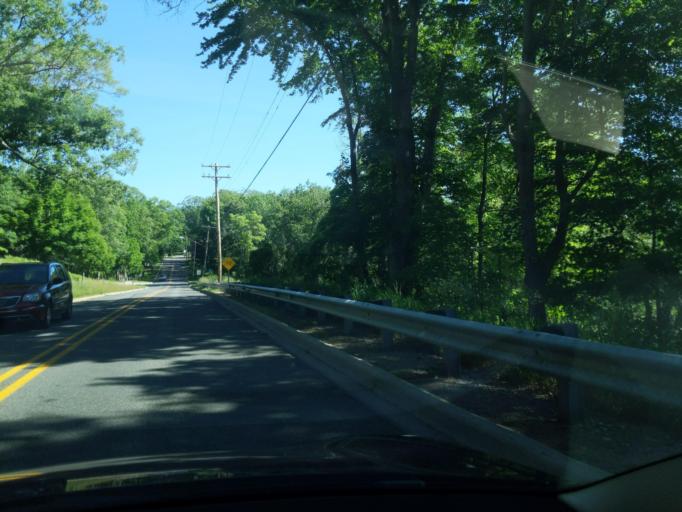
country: US
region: Michigan
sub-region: Muskegon County
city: Montague
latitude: 43.4082
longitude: -86.3602
